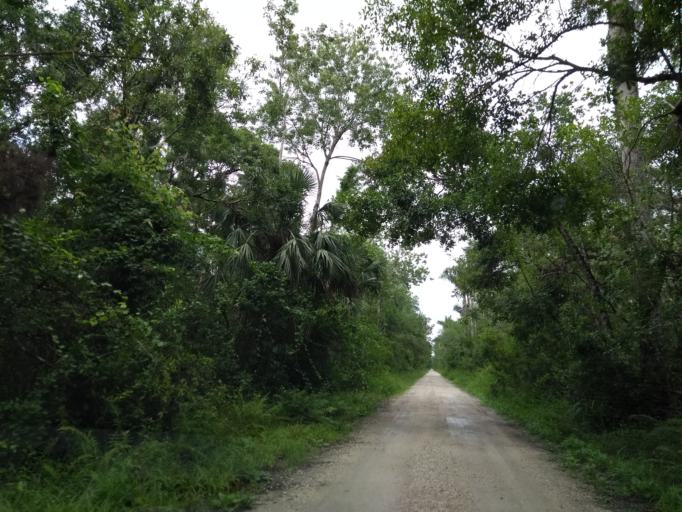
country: US
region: Florida
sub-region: Collier County
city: Lely Resort
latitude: 26.0020
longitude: -81.4112
